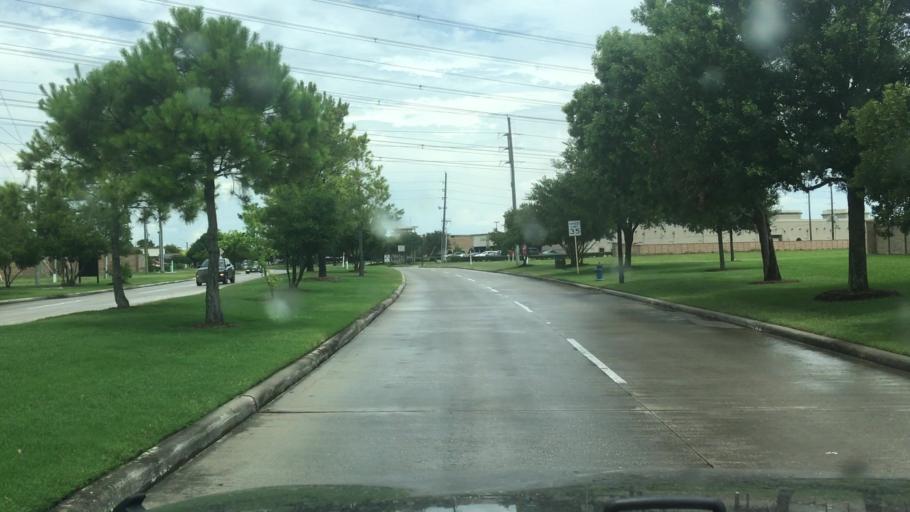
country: US
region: Texas
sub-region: Harris County
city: Humble
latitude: 29.9311
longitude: -95.2504
